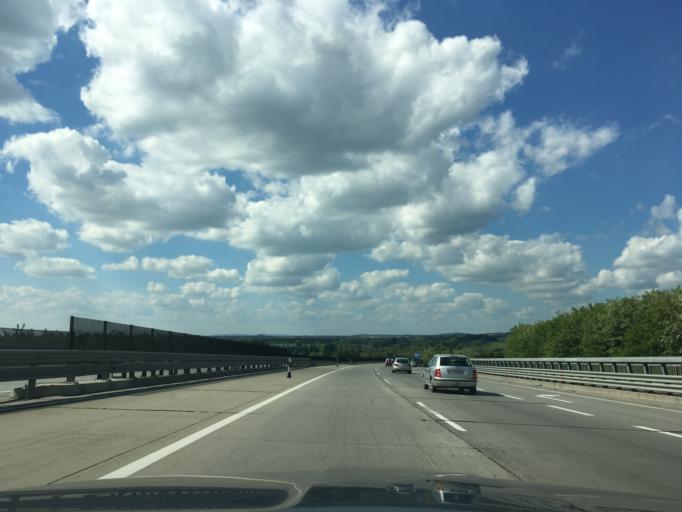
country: HU
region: Pest
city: Pecel
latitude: 47.4859
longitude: 19.3135
